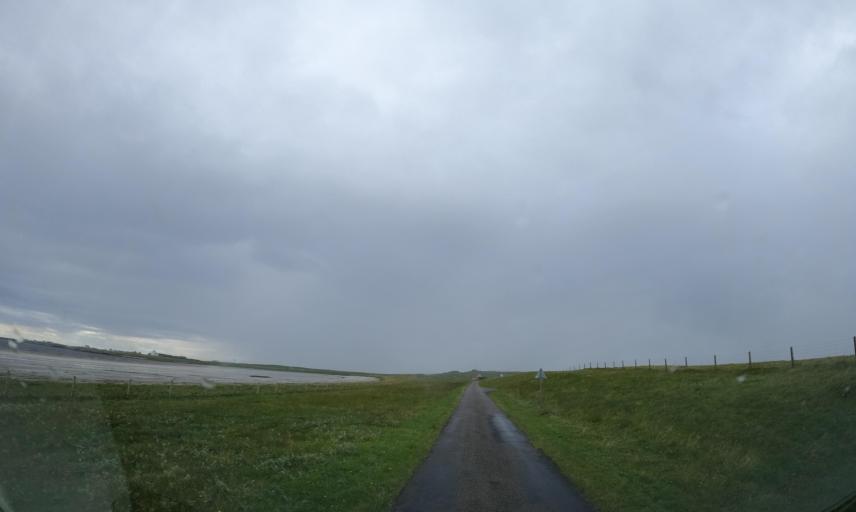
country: GB
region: Scotland
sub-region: Eilean Siar
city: Barra
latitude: 56.5176
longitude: -6.8131
